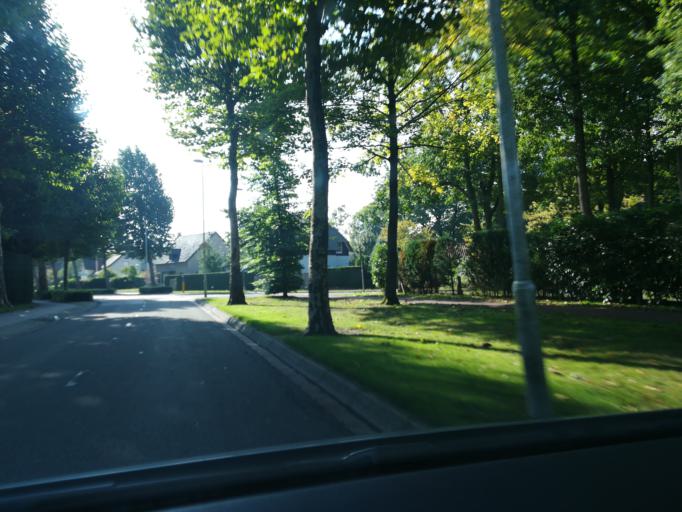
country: NL
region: North Brabant
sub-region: Gemeente Waalre
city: Waalre
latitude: 51.3952
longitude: 5.4682
